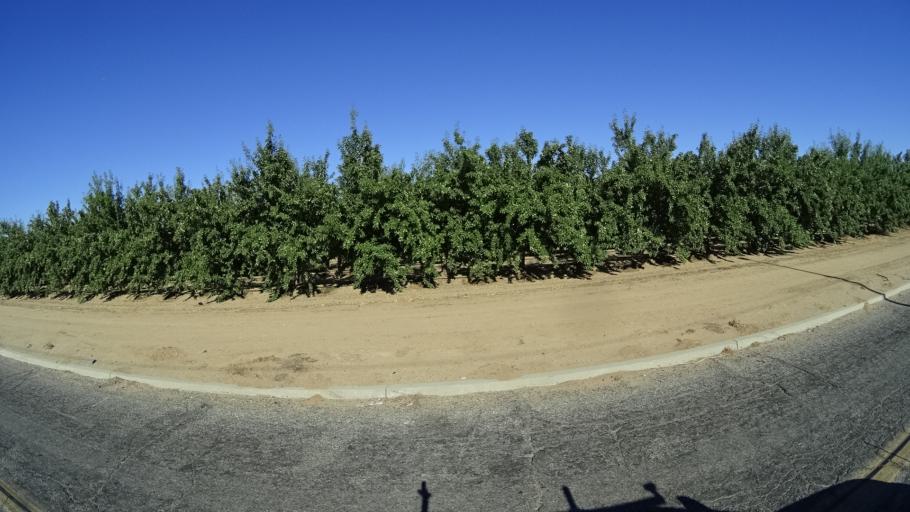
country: US
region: California
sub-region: Fresno County
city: West Park
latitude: 36.7162
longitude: -119.8267
